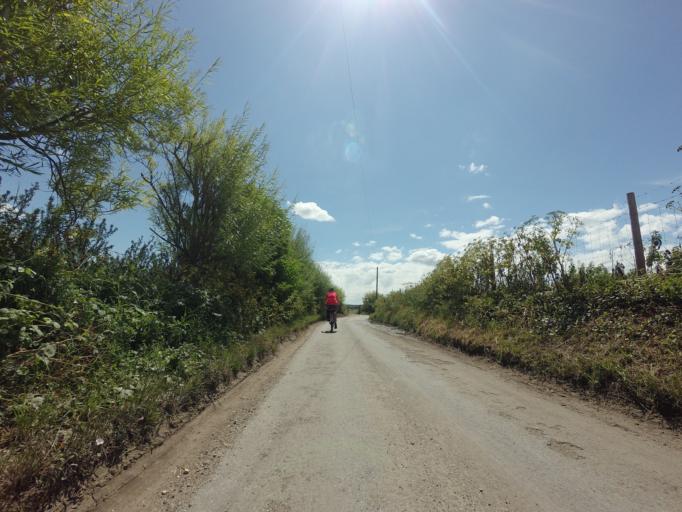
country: GB
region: England
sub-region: Medway
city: Cooling
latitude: 51.4580
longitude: 0.5138
